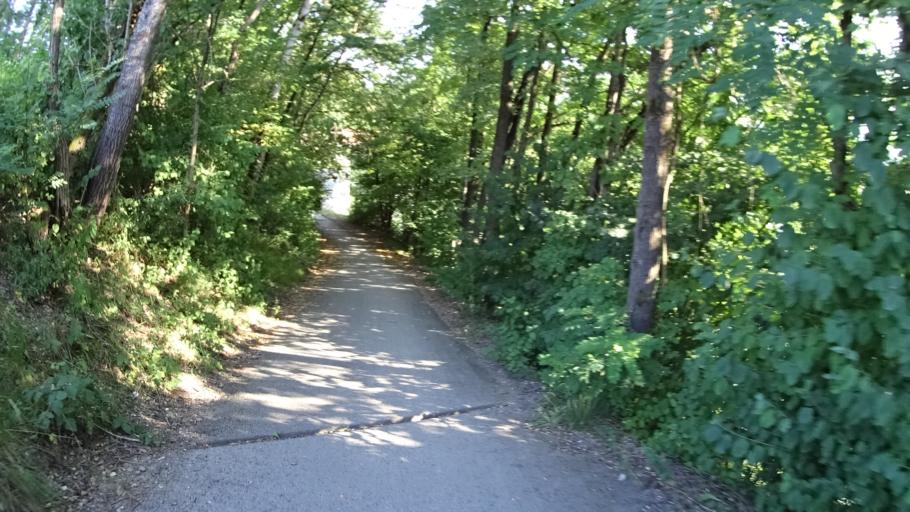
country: AT
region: Carinthia
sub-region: Politischer Bezirk Villach Land
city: Wernberg
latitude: 46.5980
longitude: 13.9513
